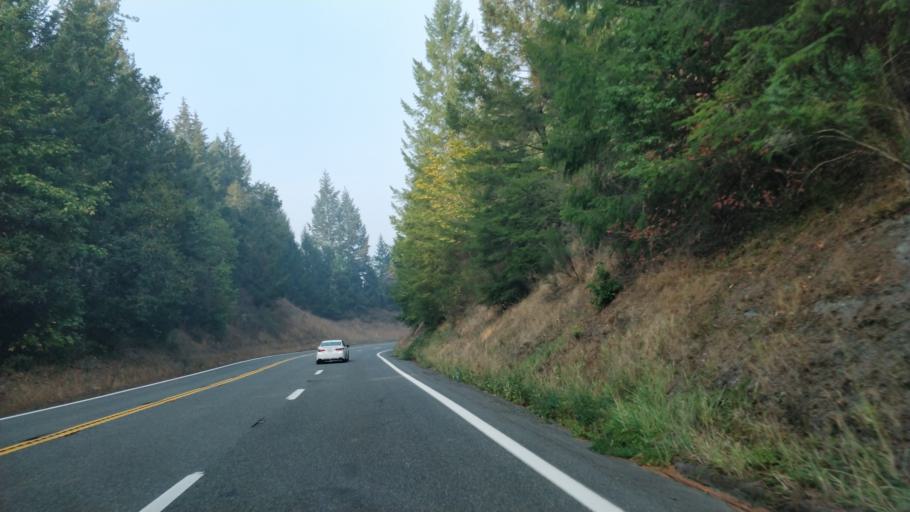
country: US
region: California
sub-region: Humboldt County
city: Blue Lake
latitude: 40.9115
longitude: -123.8090
